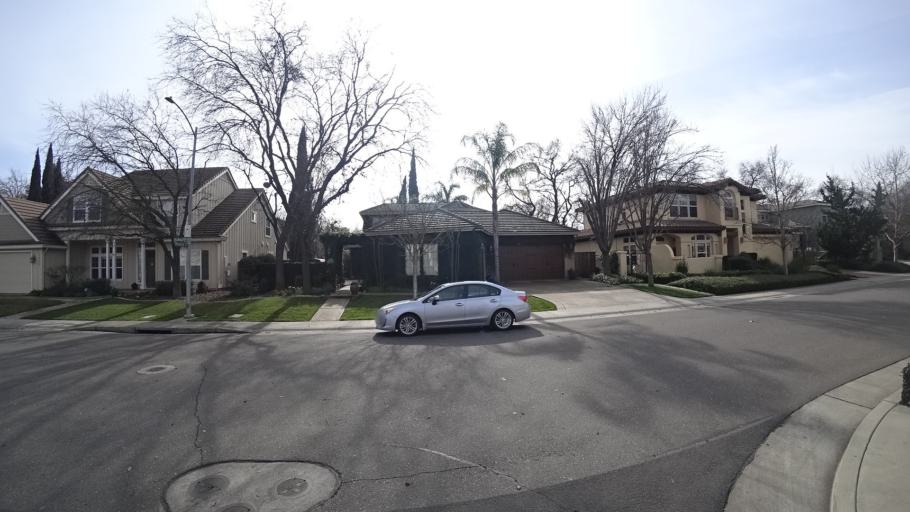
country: US
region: California
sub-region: Yolo County
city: Davis
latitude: 38.5487
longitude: -121.6818
